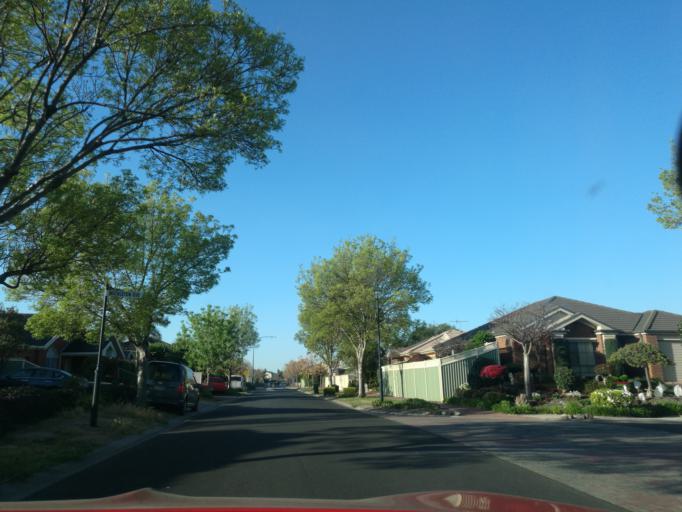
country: AU
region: Victoria
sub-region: Wyndham
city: Point Cook
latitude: -37.8924
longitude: 144.7484
